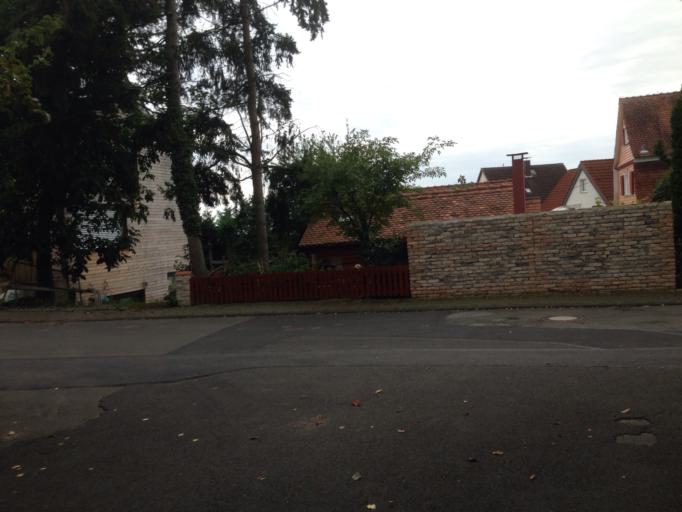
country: DE
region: Hesse
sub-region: Regierungsbezirk Giessen
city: Alten Buseck
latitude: 50.6242
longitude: 8.7532
